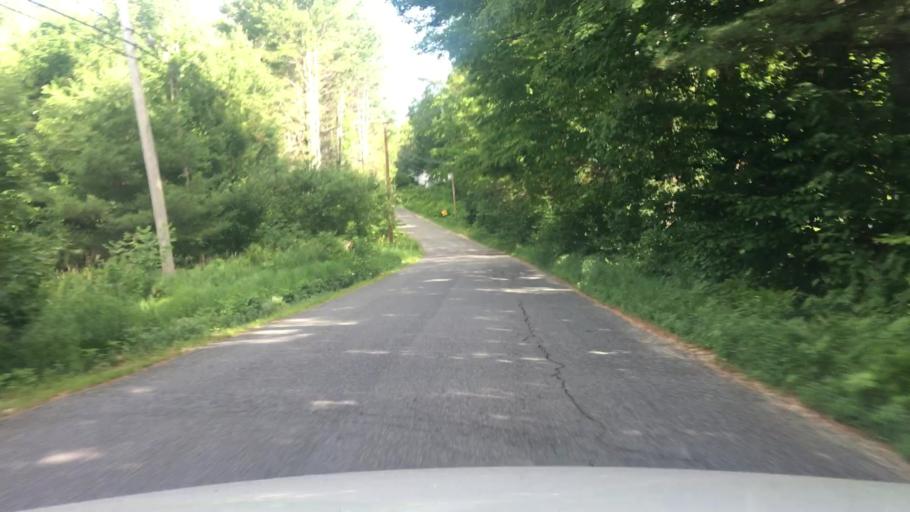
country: US
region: Maine
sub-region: Franklin County
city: Wilton
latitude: 44.6014
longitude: -70.2237
